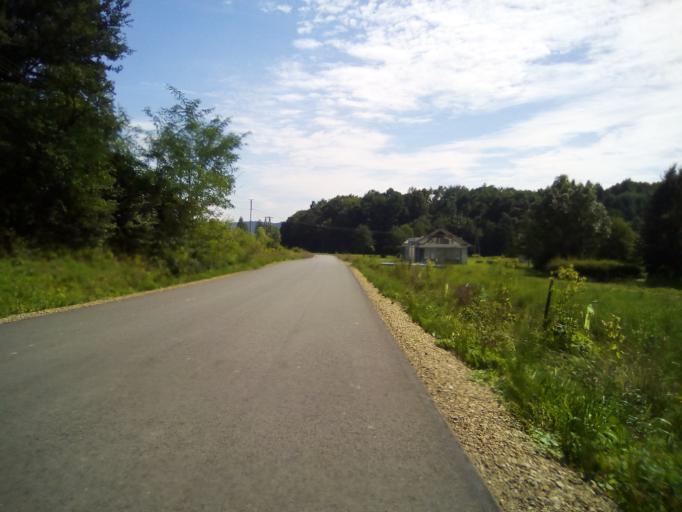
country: PL
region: Subcarpathian Voivodeship
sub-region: Powiat strzyzowski
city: Konieczkowa
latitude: 49.8124
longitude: 21.9236
